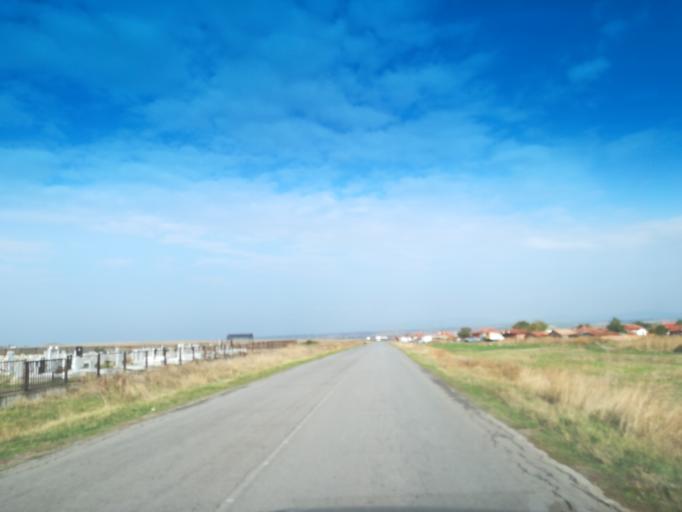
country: BG
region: Stara Zagora
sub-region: Obshtina Chirpan
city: Chirpan
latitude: 42.1989
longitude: 25.3108
